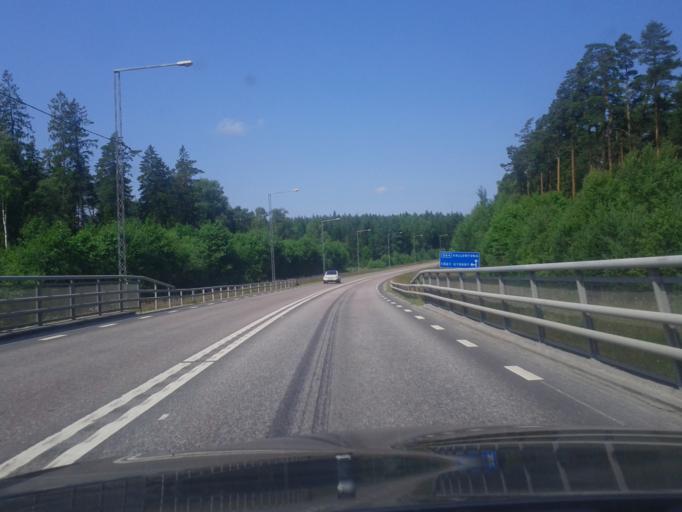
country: SE
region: Stockholm
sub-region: Vallentuna Kommun
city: Vallentuna
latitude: 59.4958
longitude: 18.1038
